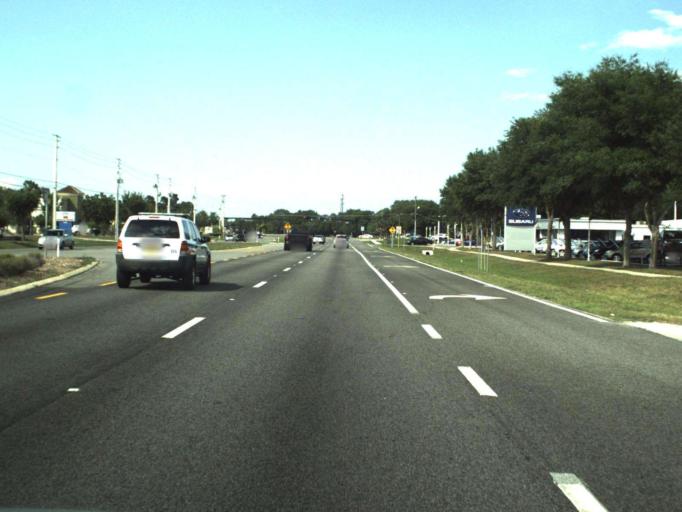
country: US
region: Florida
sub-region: Seminole County
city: Lake Mary
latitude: 28.7483
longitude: -81.2926
